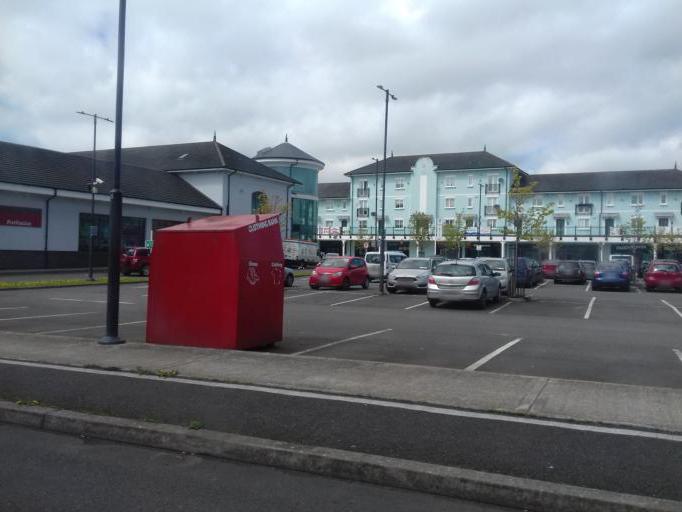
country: IE
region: Leinster
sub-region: Laois
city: Portlaoise
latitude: 53.0499
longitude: -7.3219
